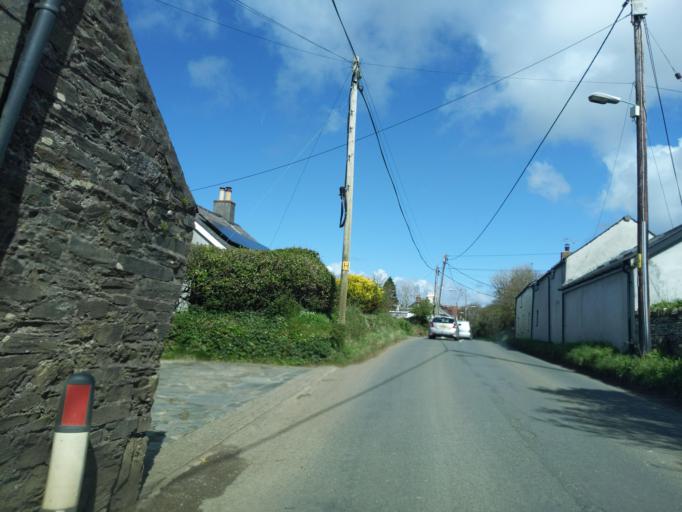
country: GB
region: England
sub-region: Cornwall
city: Wadebridge
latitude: 50.5804
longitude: -4.7934
